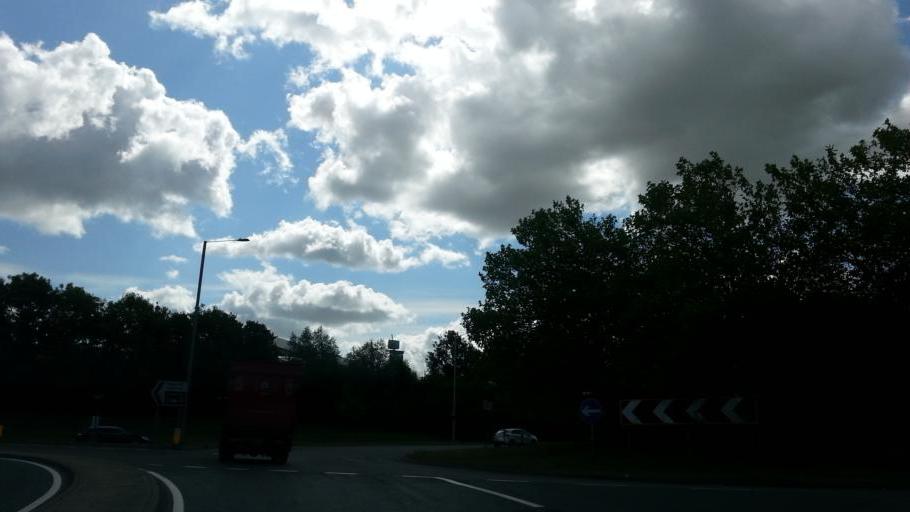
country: GB
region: England
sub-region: Essex
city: Basildon
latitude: 51.5838
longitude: 0.4415
